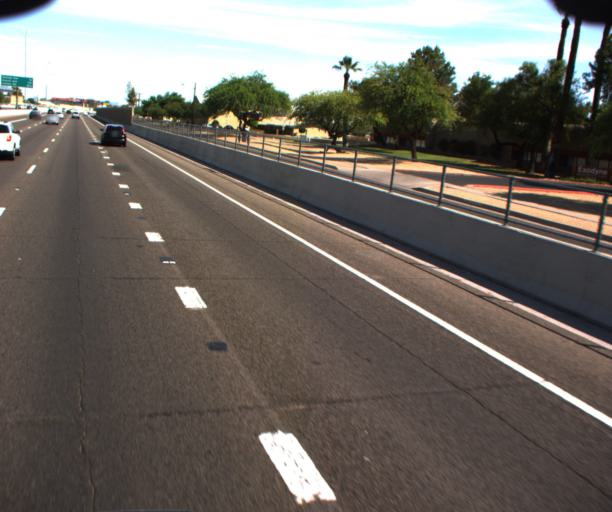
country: US
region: Arizona
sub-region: Maricopa County
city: Glendale
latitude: 33.5593
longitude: -112.1139
